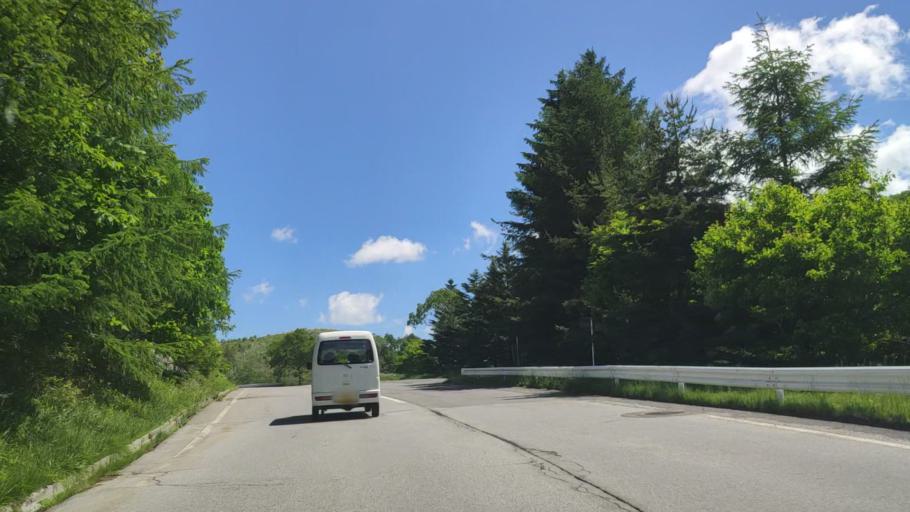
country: JP
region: Nagano
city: Chino
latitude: 36.0990
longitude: 138.2256
